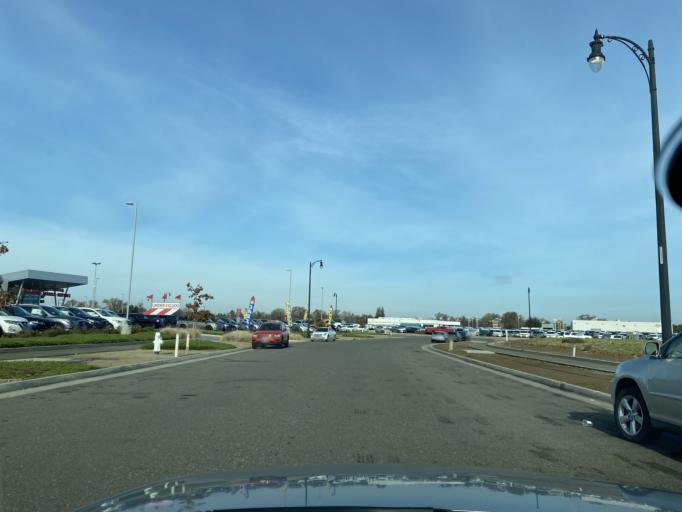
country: US
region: California
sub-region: Sacramento County
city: Elk Grove
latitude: 38.4025
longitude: -121.3915
